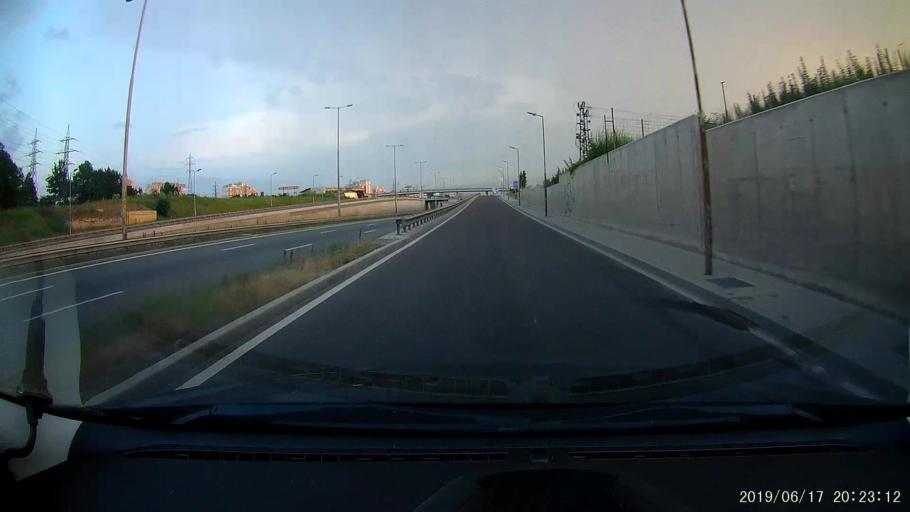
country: BG
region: Sofiya
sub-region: Obshtina Bozhurishte
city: Bozhurishte
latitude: 42.7372
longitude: 23.2488
